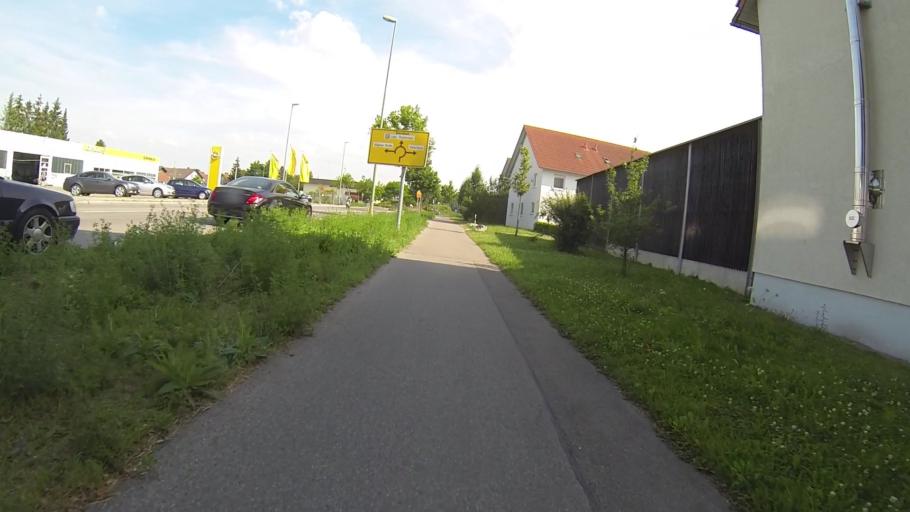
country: DE
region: Bavaria
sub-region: Swabia
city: Neu-Ulm
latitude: 48.3646
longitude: 10.0104
